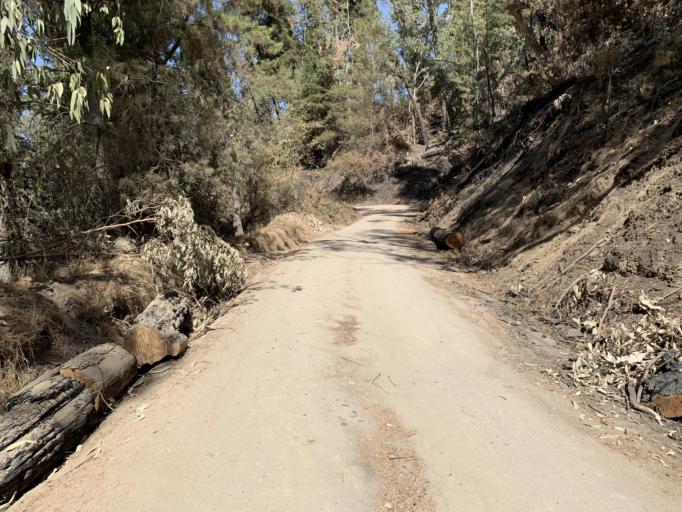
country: CL
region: Maule
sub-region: Provincia de Talca
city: Talca
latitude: -35.4178
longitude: -71.6849
